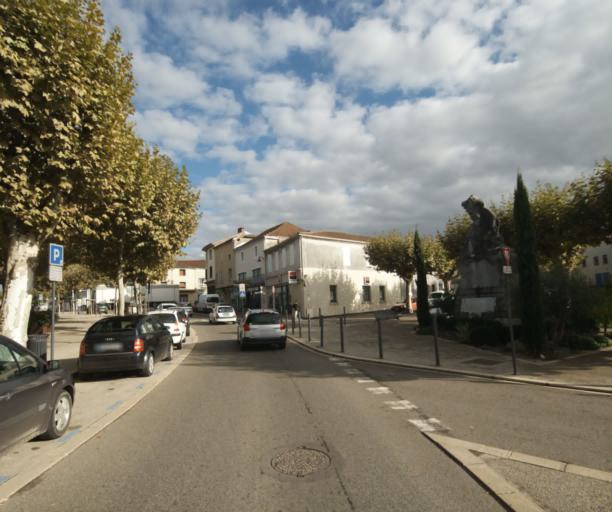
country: FR
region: Midi-Pyrenees
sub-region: Departement du Gers
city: Eauze
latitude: 43.8595
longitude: 0.0996
